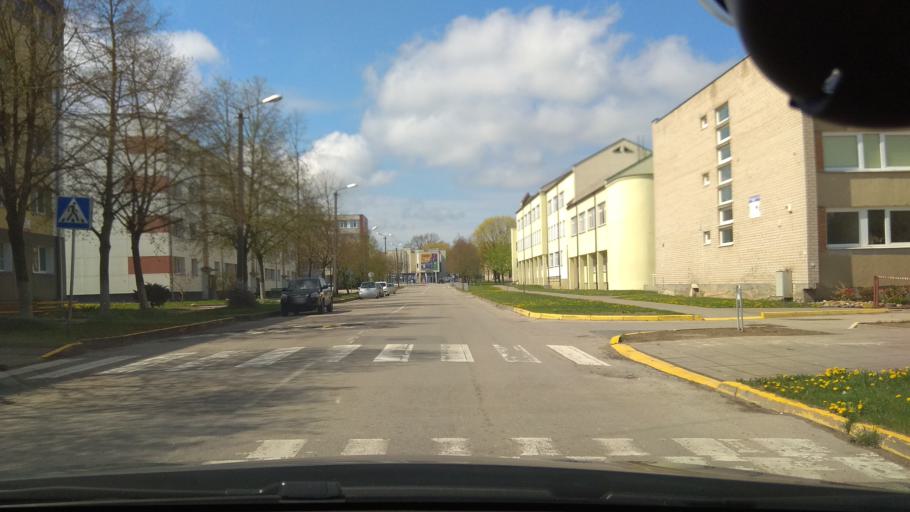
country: LT
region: Siauliu apskritis
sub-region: Joniskis
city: Joniskis
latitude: 56.2424
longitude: 23.6208
